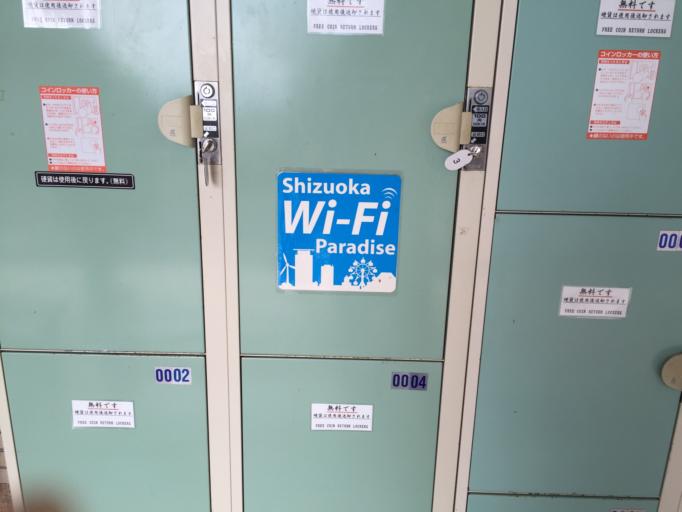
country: JP
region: Shizuoka
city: Shizuoka-shi
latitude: 34.9639
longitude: 138.4666
